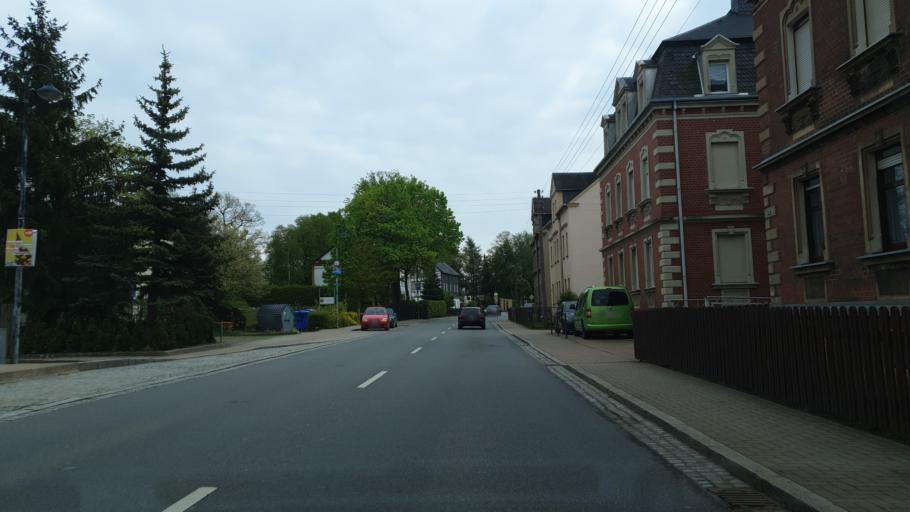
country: DE
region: Saxony
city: Lugau
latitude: 50.7445
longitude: 12.7463
